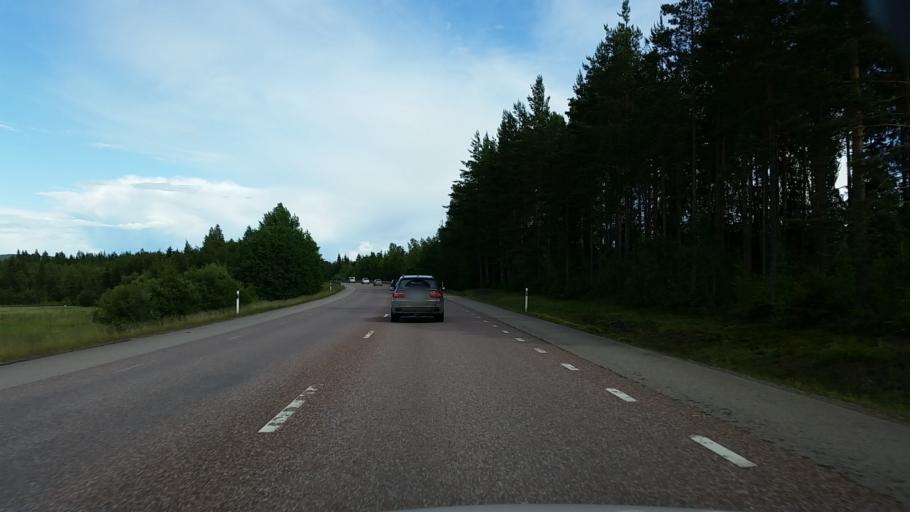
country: SE
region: Dalarna
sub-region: Smedjebackens Kommun
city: Smedjebacken
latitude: 60.0957
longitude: 15.5135
